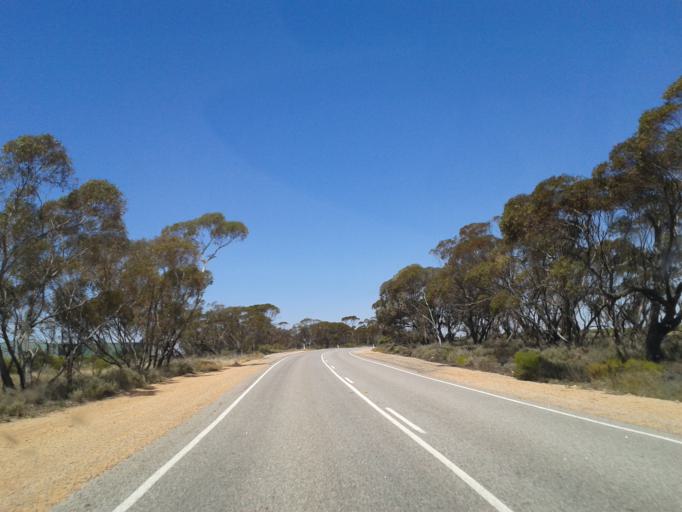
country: AU
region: Victoria
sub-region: Mildura Shire
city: Ouyen
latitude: -34.6542
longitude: 142.8328
